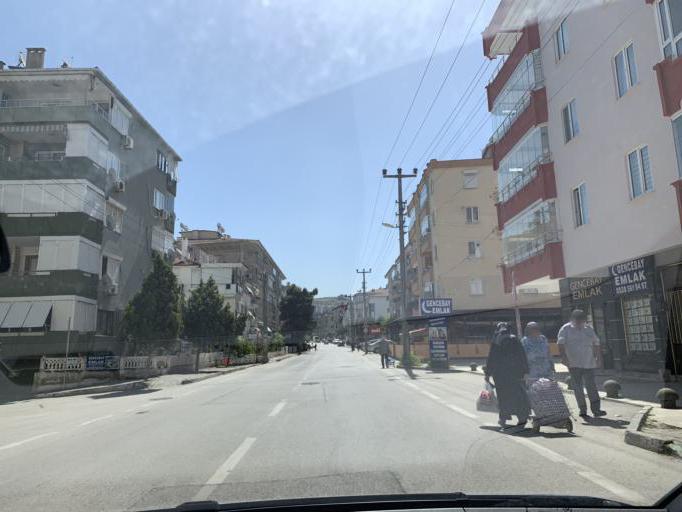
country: TR
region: Bursa
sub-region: Mudanya
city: Mudanya
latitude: 40.3556
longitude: 28.9225
